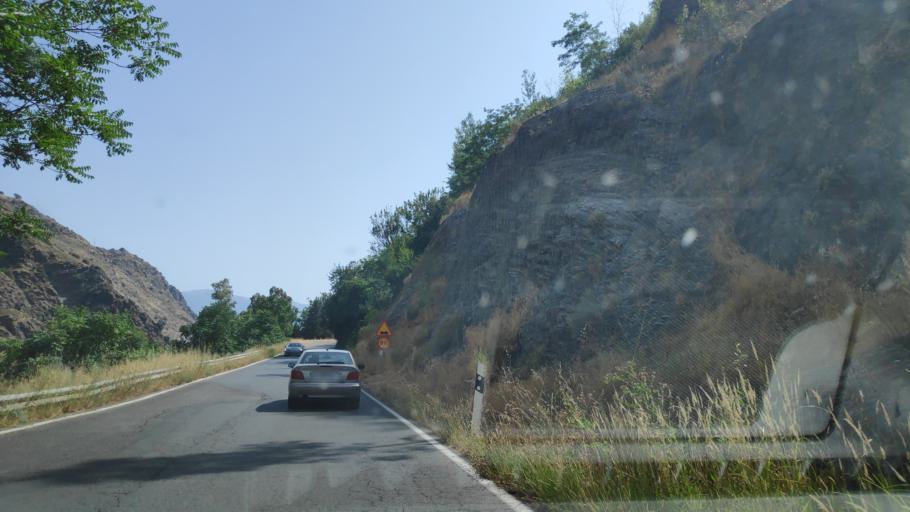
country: ES
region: Andalusia
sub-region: Provincia de Granada
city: Pampaneira
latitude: 36.9385
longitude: -3.3661
